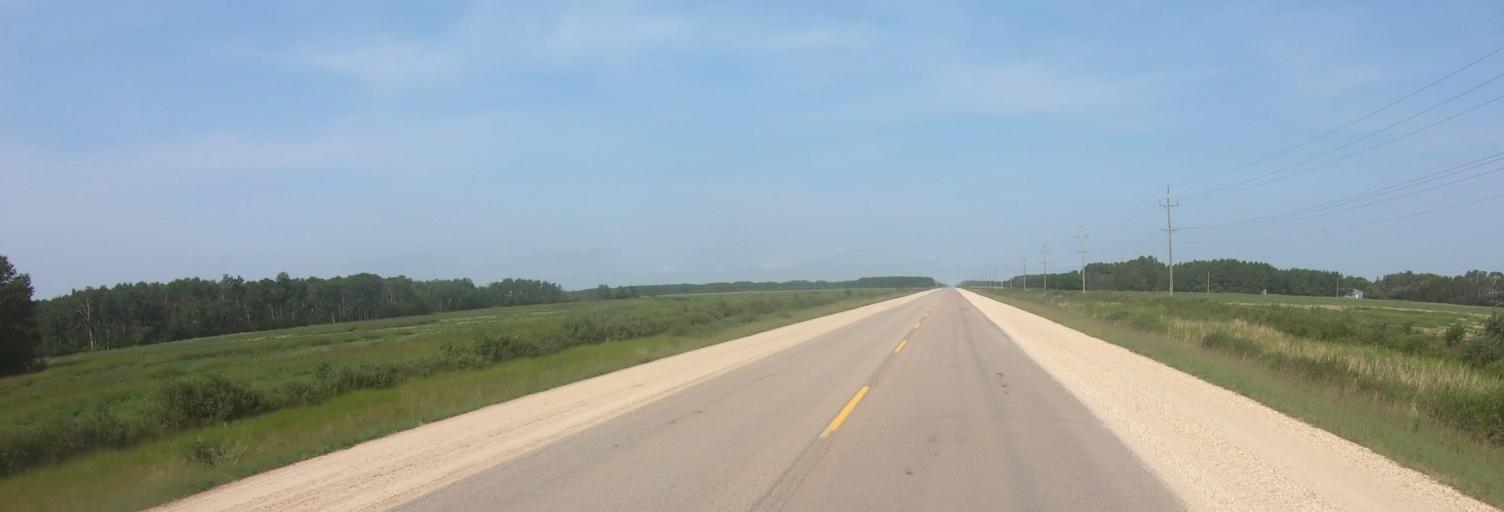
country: CA
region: Manitoba
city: La Broquerie
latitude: 49.2968
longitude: -96.5375
